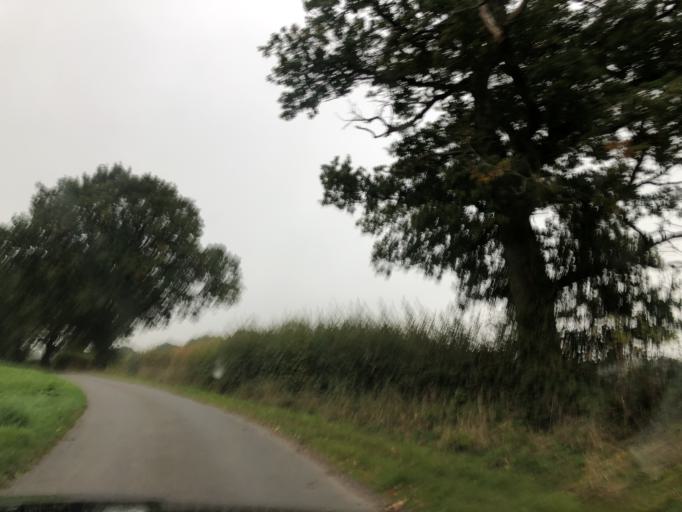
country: GB
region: England
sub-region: Warwickshire
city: Wroxall
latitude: 52.3185
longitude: -1.6565
